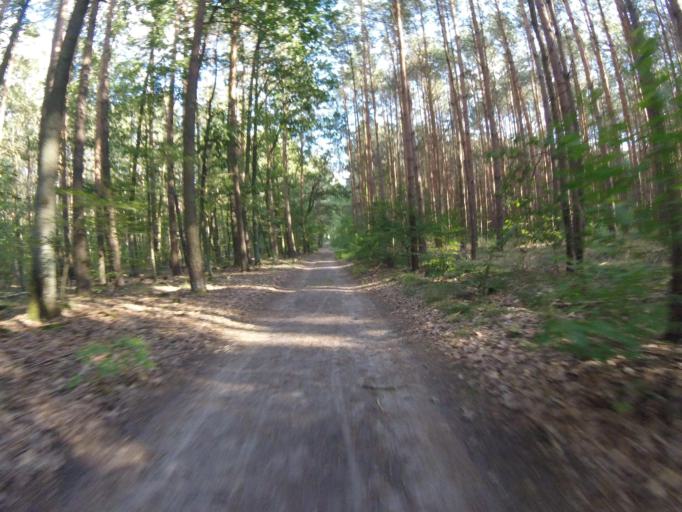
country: DE
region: Brandenburg
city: Schulzendorf
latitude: 52.3273
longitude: 13.5887
